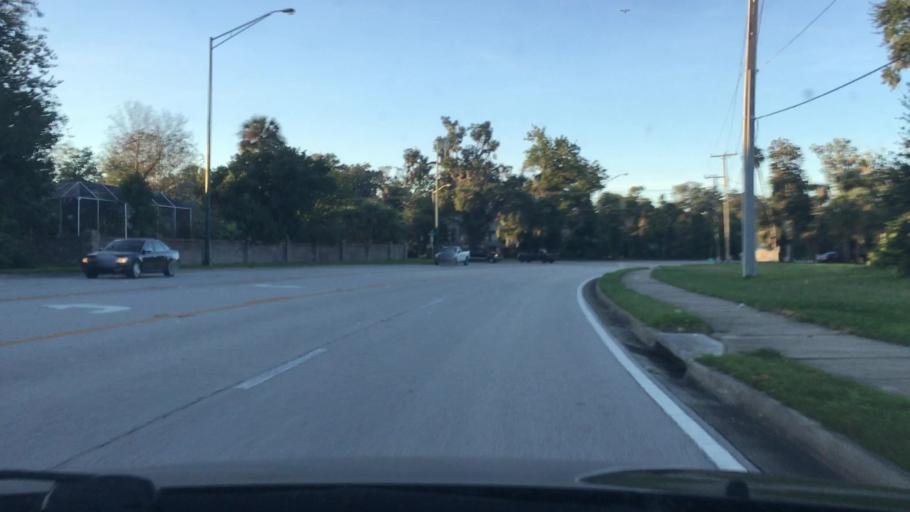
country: US
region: Florida
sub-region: Volusia County
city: Ormond Beach
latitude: 29.2933
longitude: -81.0875
